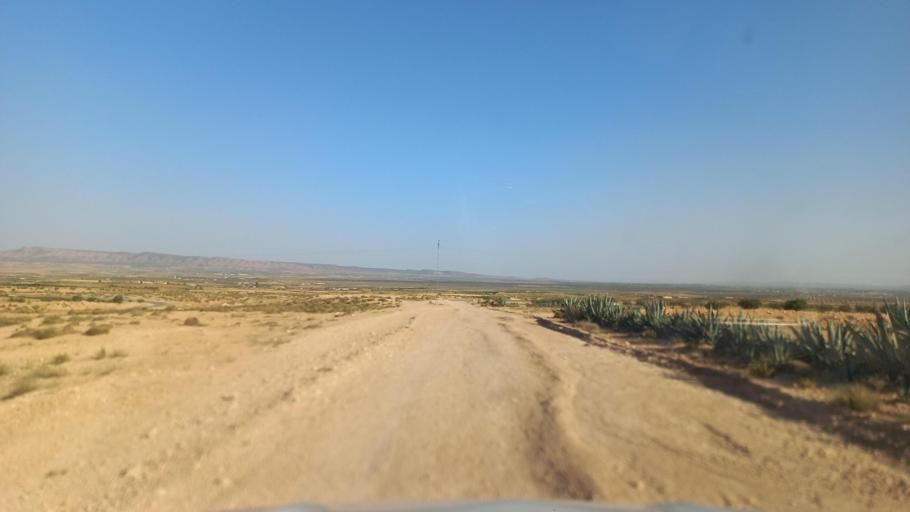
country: TN
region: Al Qasrayn
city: Sbiba
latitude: 35.3640
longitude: 8.9999
